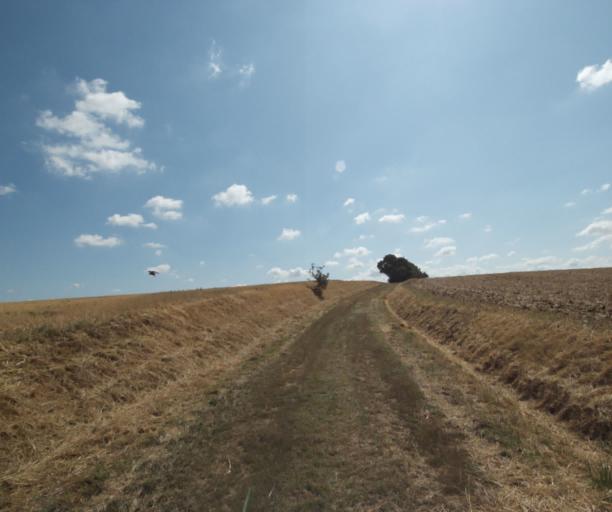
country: FR
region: Midi-Pyrenees
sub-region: Departement de la Haute-Garonne
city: Auriac-sur-Vendinelle
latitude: 43.4654
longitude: 1.8003
